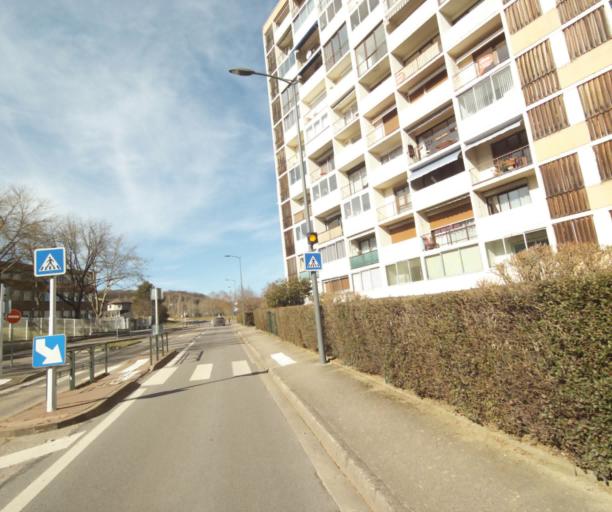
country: FR
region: Lorraine
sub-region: Departement de Meurthe-et-Moselle
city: Laxou
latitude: 48.6775
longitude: 6.1446
